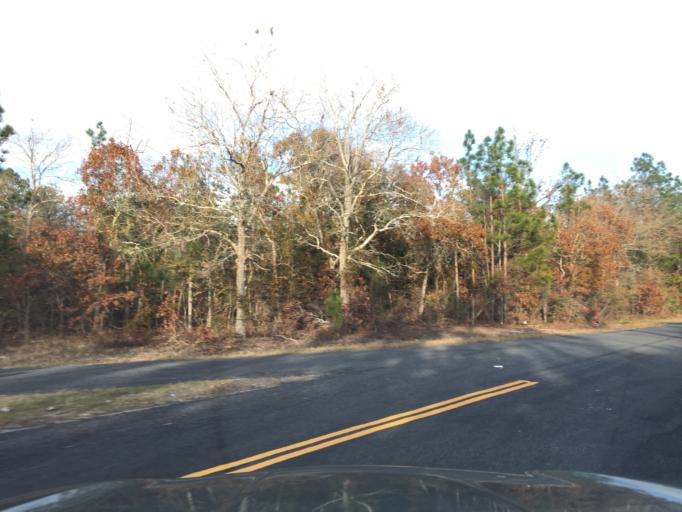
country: US
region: South Carolina
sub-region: Lexington County
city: Leesville
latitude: 33.6843
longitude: -81.3784
